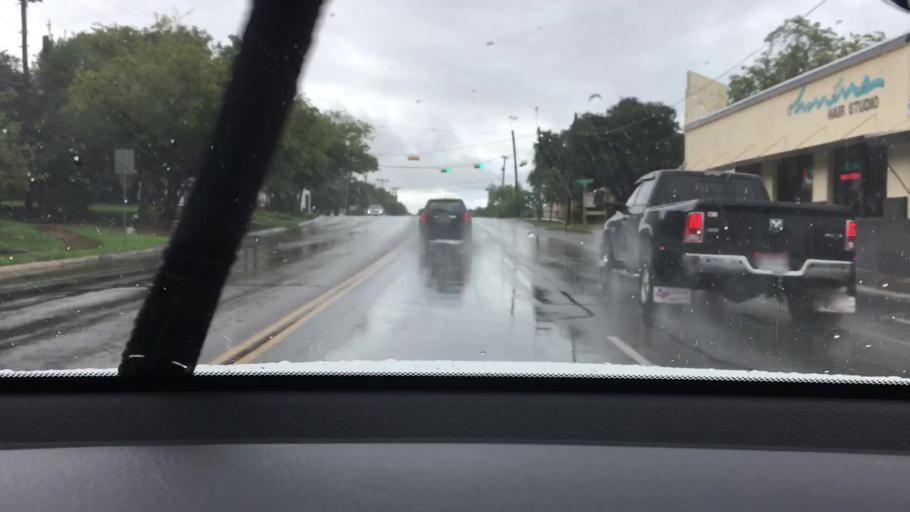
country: US
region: Texas
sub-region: Bexar County
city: Alamo Heights
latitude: 29.4858
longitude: -98.4665
